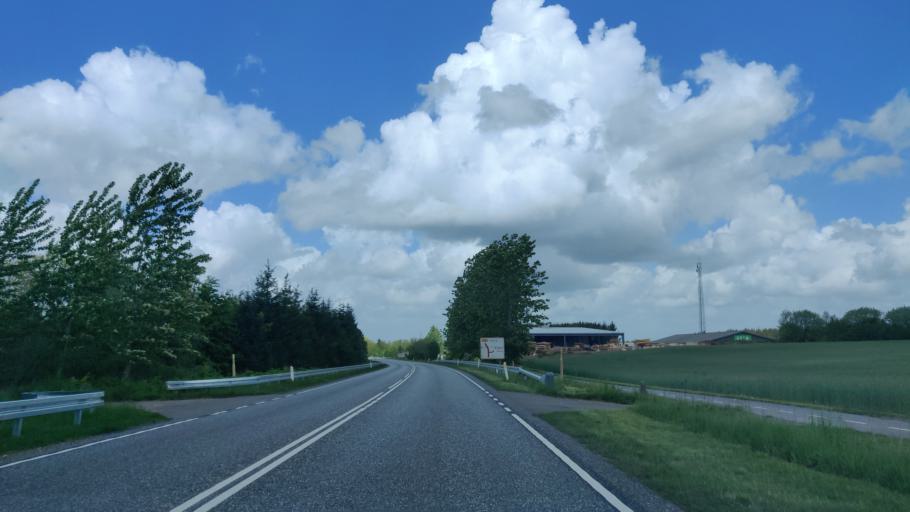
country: DK
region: Central Jutland
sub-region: Ikast-Brande Kommune
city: Bording Kirkeby
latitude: 56.1572
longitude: 9.3510
